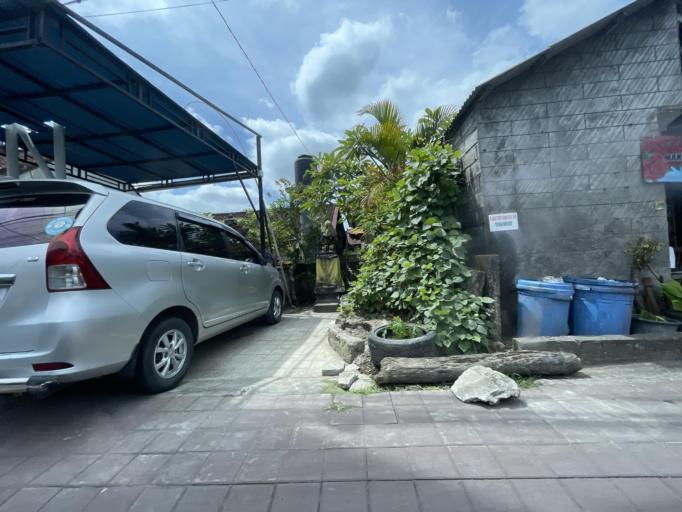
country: ID
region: Bali
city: Kuta
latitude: -8.6715
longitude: 115.1601
